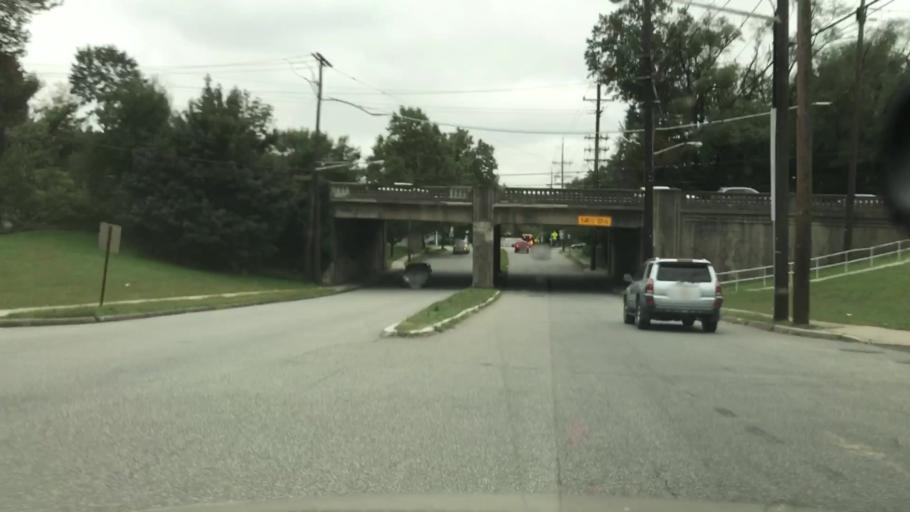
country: US
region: New Jersey
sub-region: Bergen County
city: Englewood
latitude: 40.8773
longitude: -73.9768
